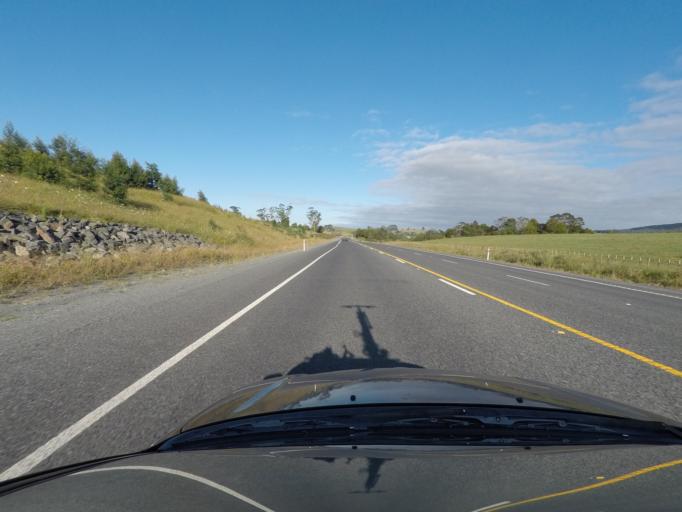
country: NZ
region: Northland
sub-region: Far North District
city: Kawakawa
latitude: -35.4992
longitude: 174.1699
